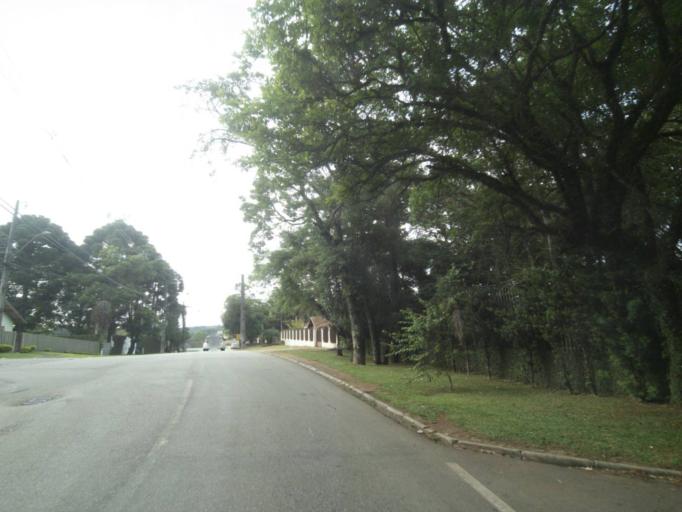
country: BR
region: Parana
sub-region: Curitiba
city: Curitiba
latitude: -25.4158
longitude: -49.3203
